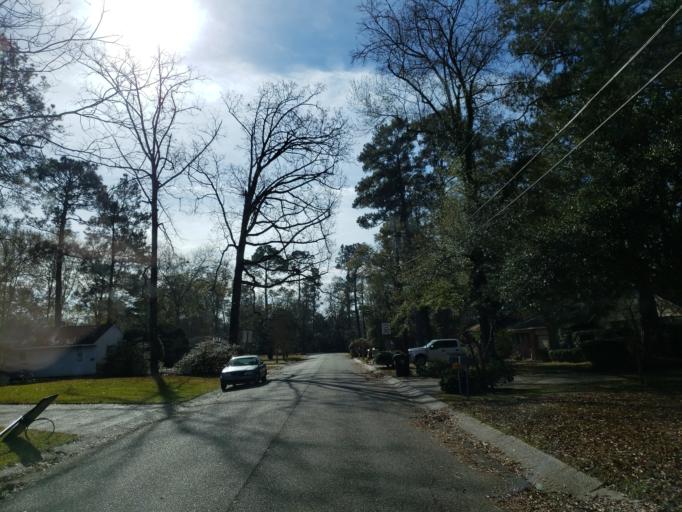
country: US
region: Mississippi
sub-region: Lamar County
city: West Hattiesburg
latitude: 31.3082
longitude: -89.3349
